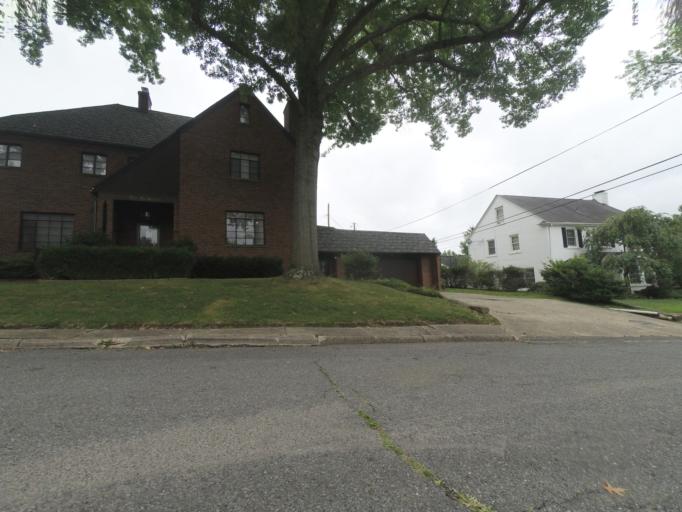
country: US
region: West Virginia
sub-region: Cabell County
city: Huntington
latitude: 38.4044
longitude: -82.4160
